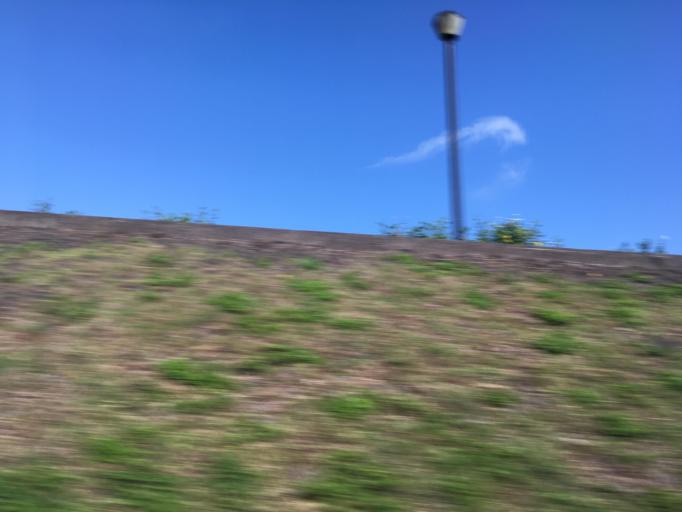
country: TW
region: Taiwan
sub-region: Yilan
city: Yilan
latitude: 24.7508
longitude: 121.7285
